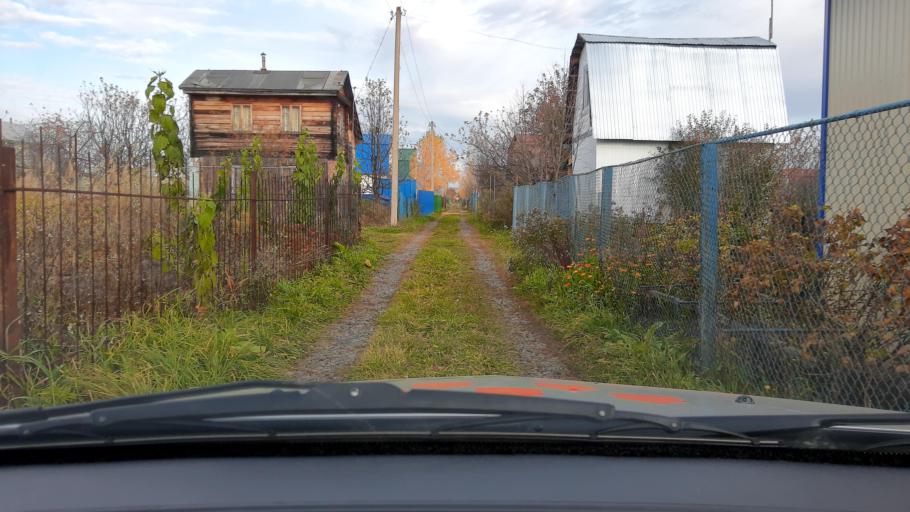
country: RU
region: Bashkortostan
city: Asanovo
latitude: 54.8022
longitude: 55.6134
